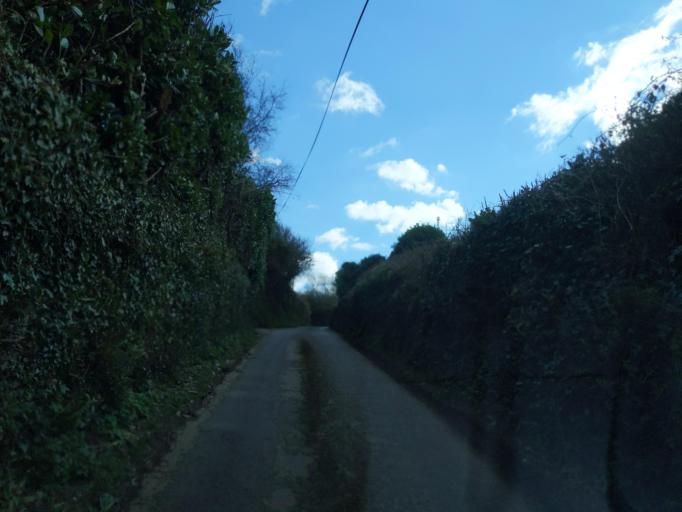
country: GB
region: England
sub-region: Devon
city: Salcombe
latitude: 50.2508
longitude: -3.7014
